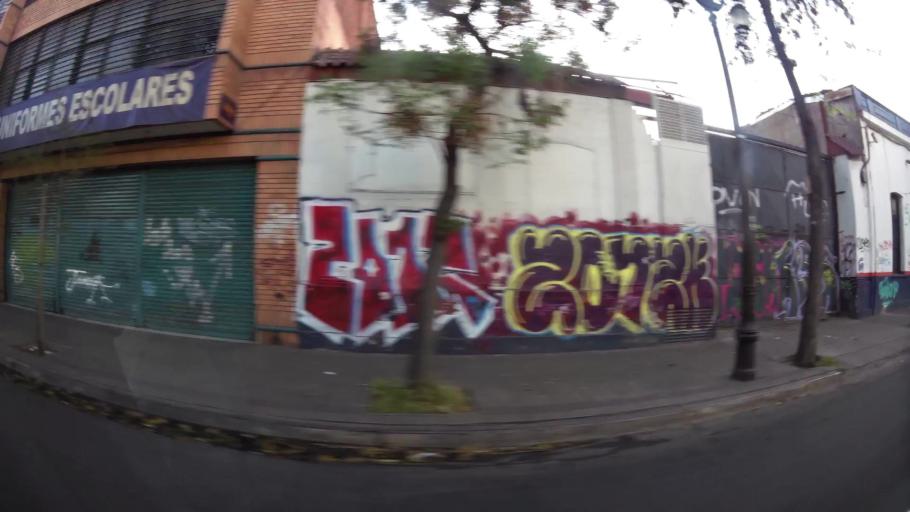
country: CL
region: Santiago Metropolitan
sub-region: Provincia de Santiago
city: Santiago
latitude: -33.4360
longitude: -70.6690
